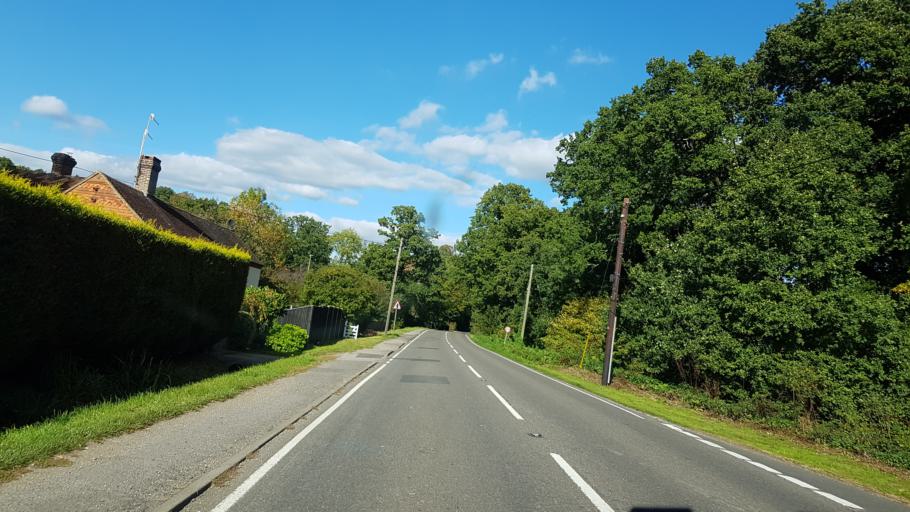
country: GB
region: England
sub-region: Surrey
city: Chiddingfold
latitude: 51.0889
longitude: -0.6453
